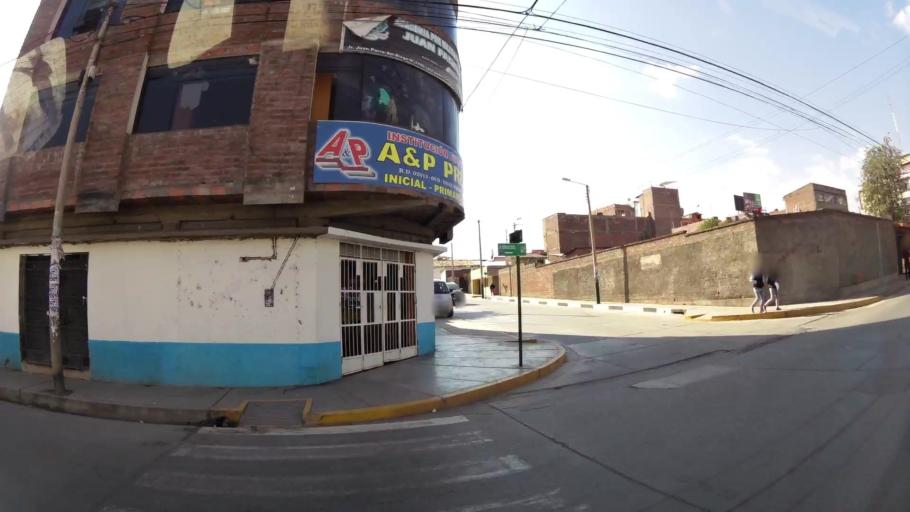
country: PE
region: Junin
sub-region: Provincia de Huancayo
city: El Tambo
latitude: -12.0634
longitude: -75.2200
